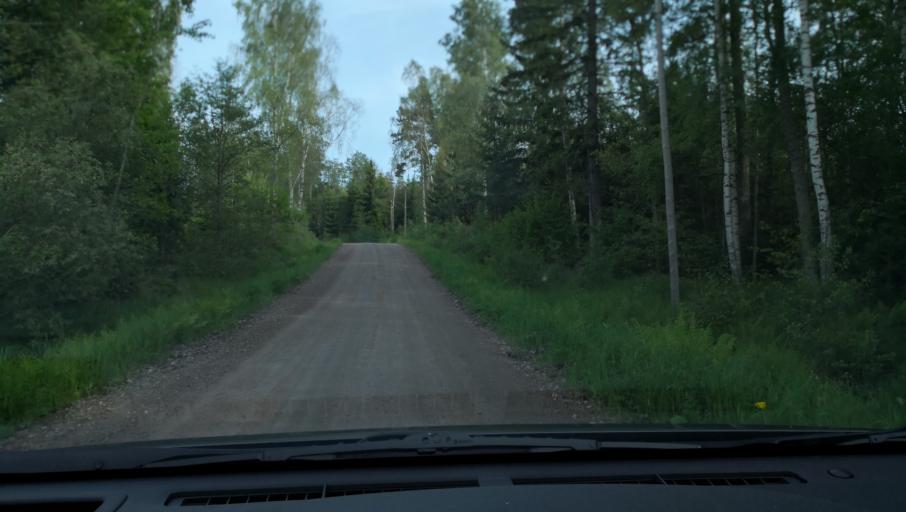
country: SE
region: Vaestmanland
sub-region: Arboga Kommun
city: Tyringe
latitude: 59.3629
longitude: 15.9612
